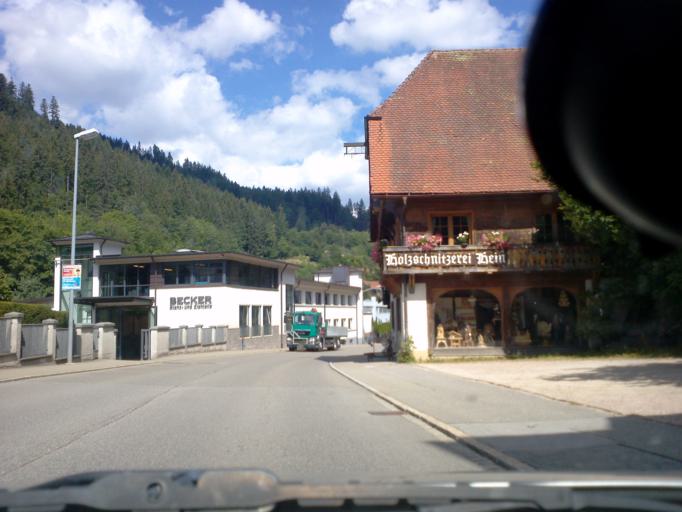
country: DE
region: Baden-Wuerttemberg
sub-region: Freiburg Region
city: Triberg im Schwarzwald
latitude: 48.1393
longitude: 8.2396
